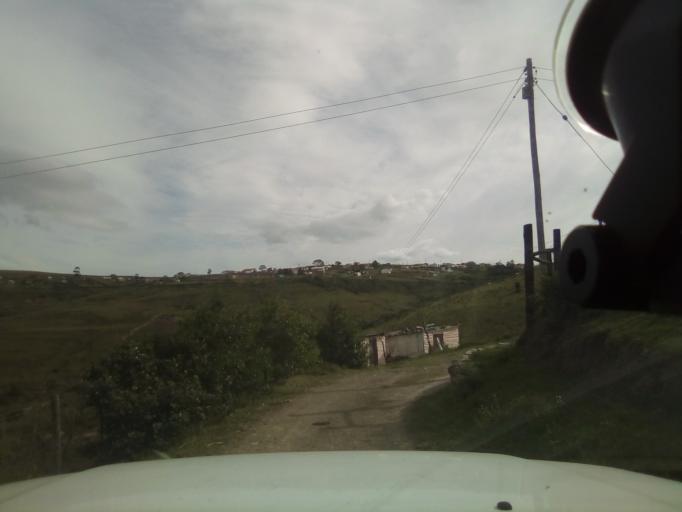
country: ZA
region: Eastern Cape
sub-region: Buffalo City Metropolitan Municipality
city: East London
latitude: -32.7967
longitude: 27.9670
